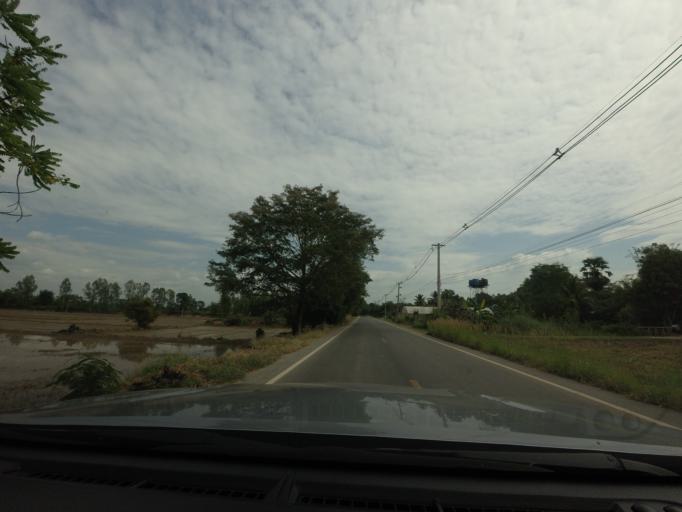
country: TH
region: Phitsanulok
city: Wang Thong
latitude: 16.7231
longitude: 100.3527
